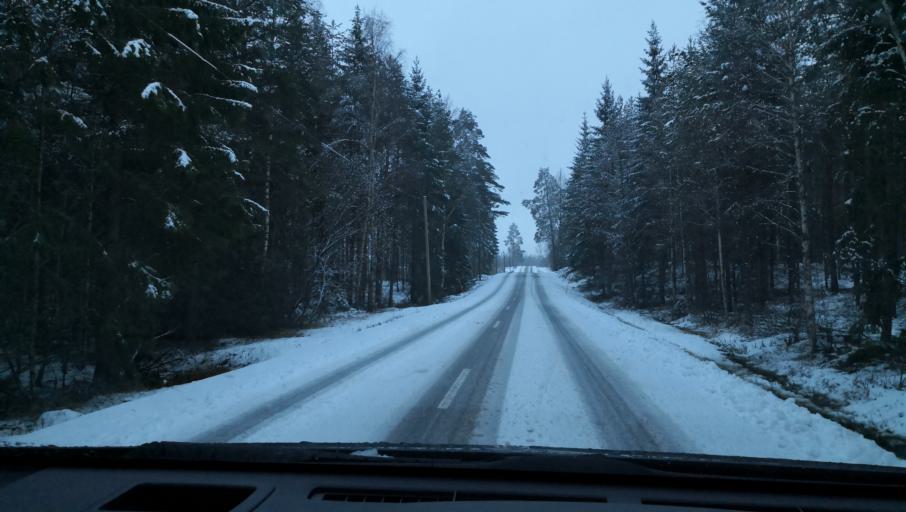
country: SE
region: Vaestmanland
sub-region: Kopings Kommun
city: Kolsva
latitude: 59.5755
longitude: 15.8002
